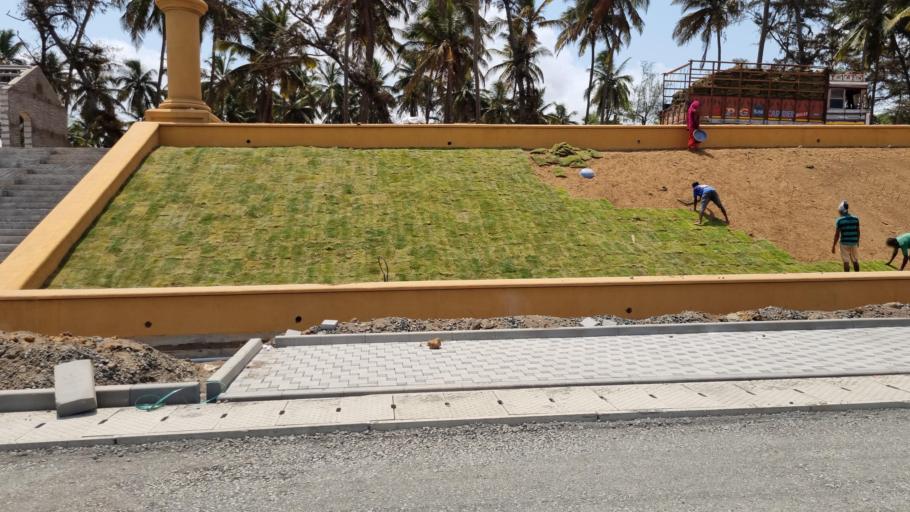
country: IN
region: Daman and Diu
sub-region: Daman District
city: Daman
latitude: 20.4444
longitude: 72.8322
